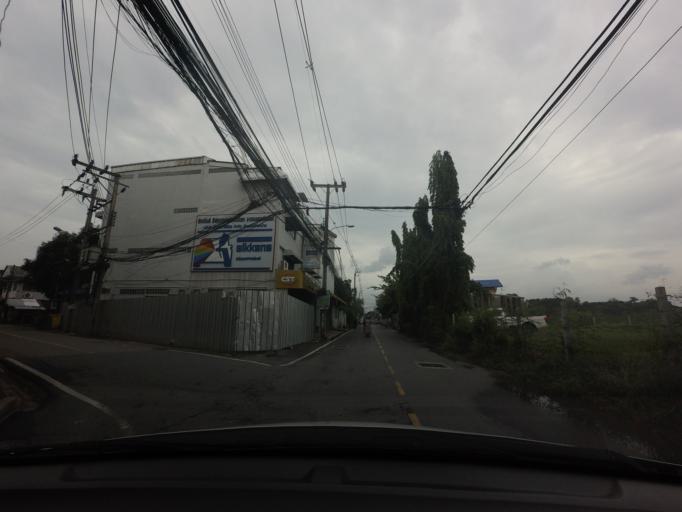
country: TH
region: Nonthaburi
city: Pak Kret
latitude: 13.9044
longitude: 100.5125
